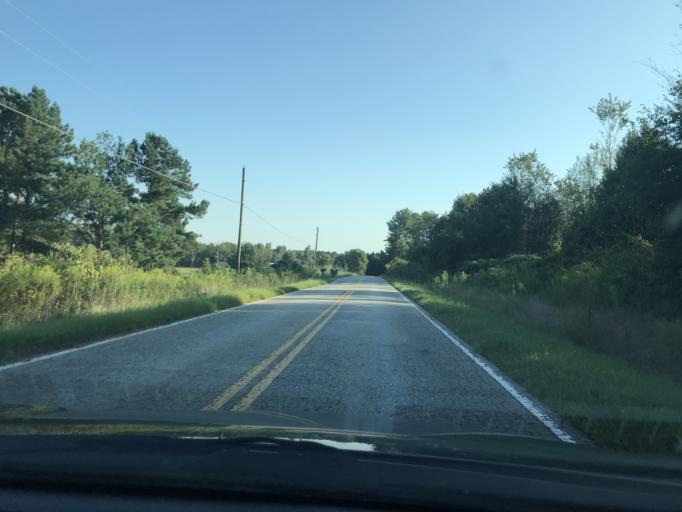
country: US
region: South Carolina
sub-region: Spartanburg County
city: Mayo
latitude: 35.1130
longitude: -81.7842
